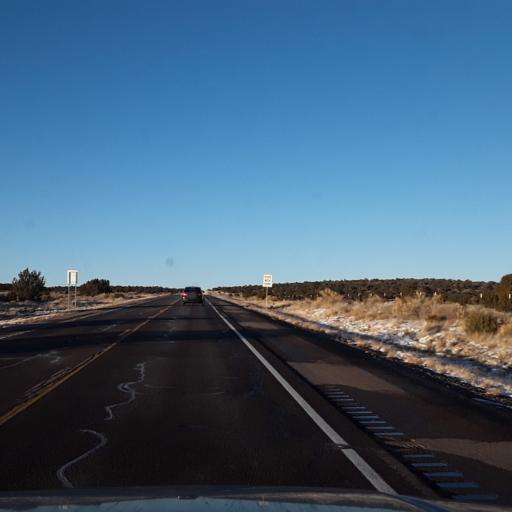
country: US
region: New Mexico
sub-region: Lincoln County
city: Carrizozo
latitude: 34.2080
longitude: -105.6483
